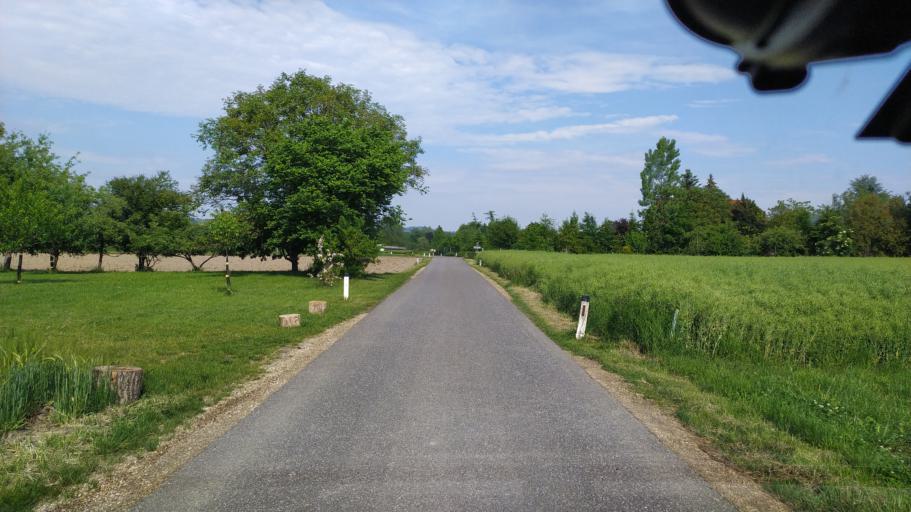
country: AT
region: Upper Austria
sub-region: Politischer Bezirk Perg
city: Bad Kreuzen
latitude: 48.1952
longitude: 14.7676
